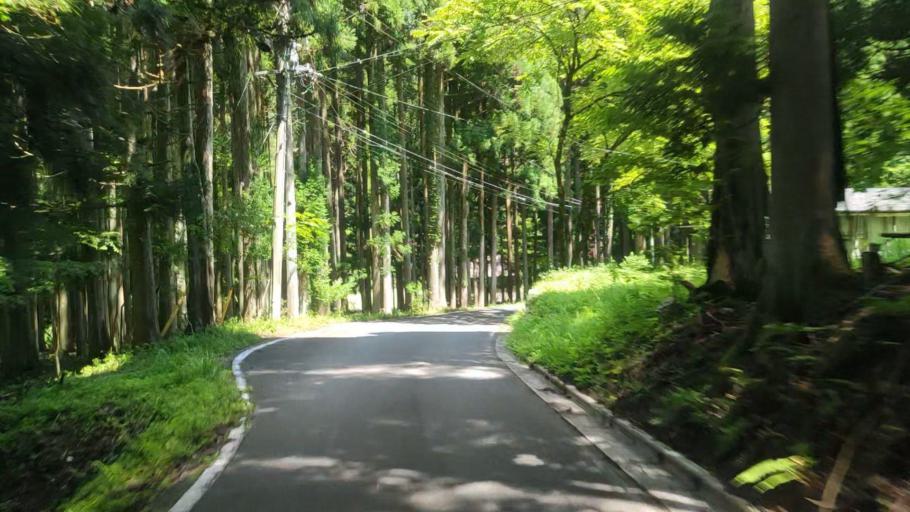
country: JP
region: Fukui
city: Ono
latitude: 35.7510
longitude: 136.5797
